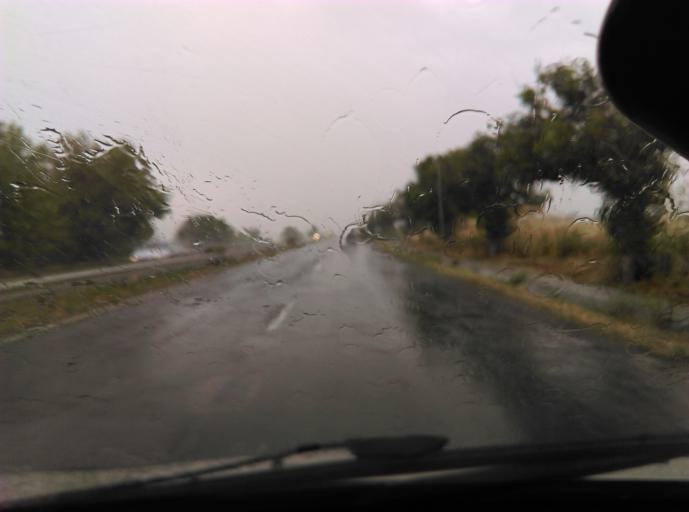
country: BG
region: Burgas
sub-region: Obshtina Burgas
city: Burgas
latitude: 42.5726
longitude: 27.4127
